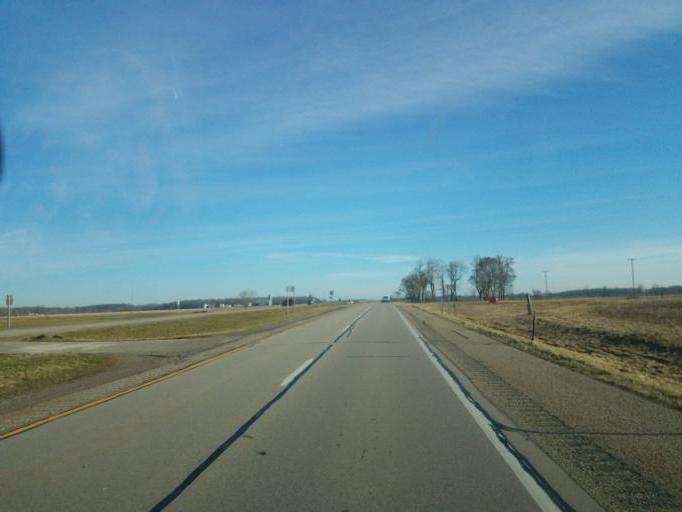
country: US
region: Michigan
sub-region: Gratiot County
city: Ithaca
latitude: 43.1530
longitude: -84.5632
